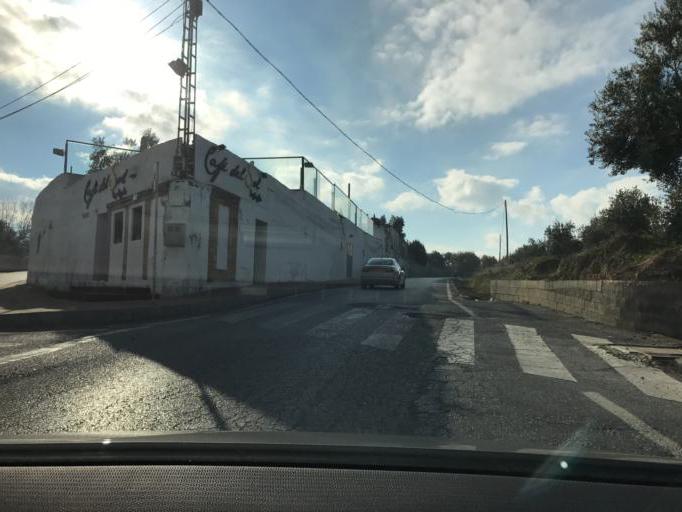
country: ES
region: Andalusia
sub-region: Provincia de Granada
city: Alhendin
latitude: 37.1020
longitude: -3.6362
